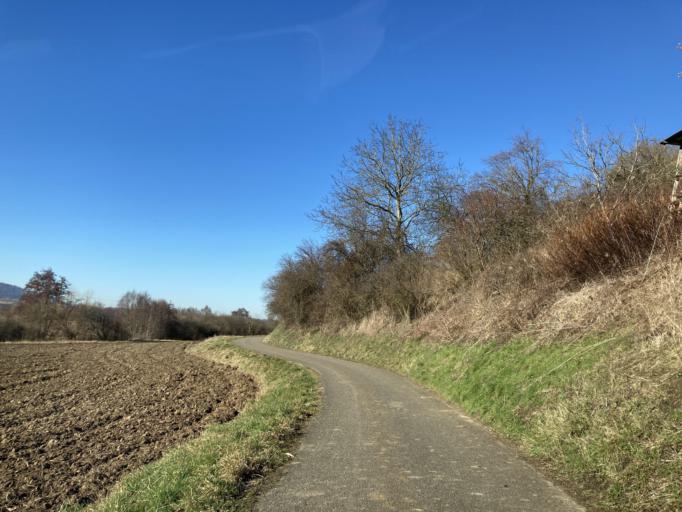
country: DE
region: Baden-Wuerttemberg
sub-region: Freiburg Region
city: Eichstetten
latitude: 48.0913
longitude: 7.7697
